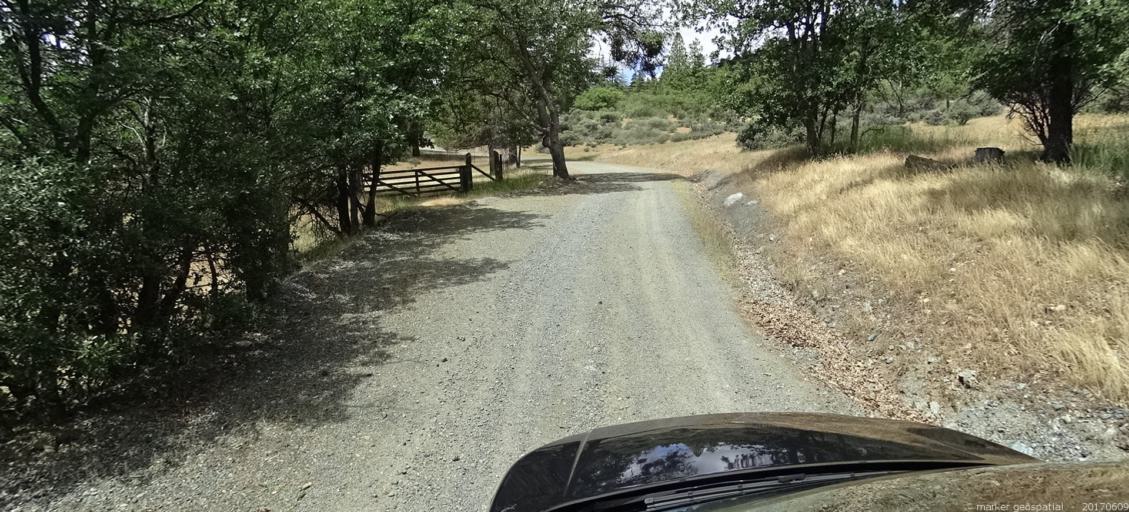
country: US
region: California
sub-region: Siskiyou County
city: Yreka
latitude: 41.3659
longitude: -122.8834
